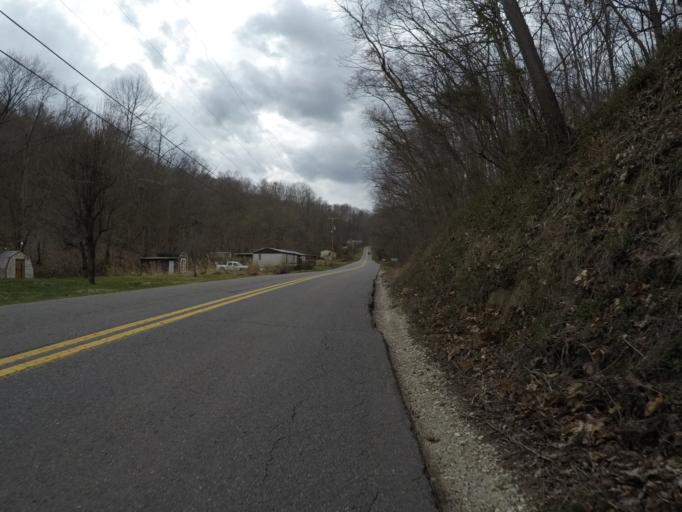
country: US
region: Ohio
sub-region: Lawrence County
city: Burlington
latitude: 38.4287
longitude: -82.5206
